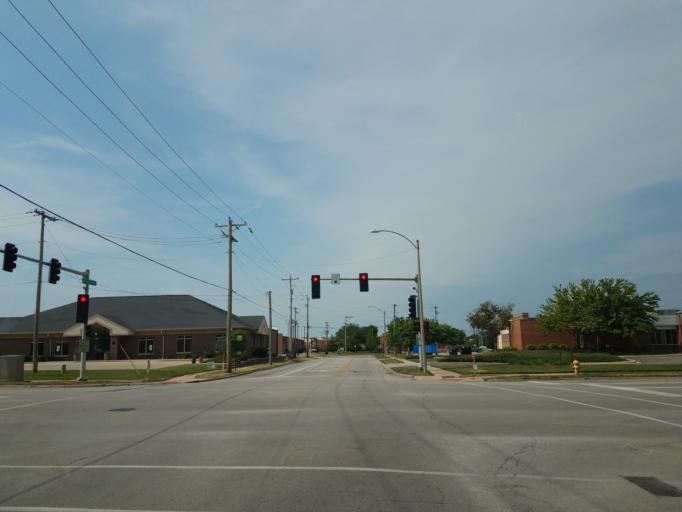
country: US
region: Illinois
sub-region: McLean County
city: Bloomington
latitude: 40.4798
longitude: -88.9503
